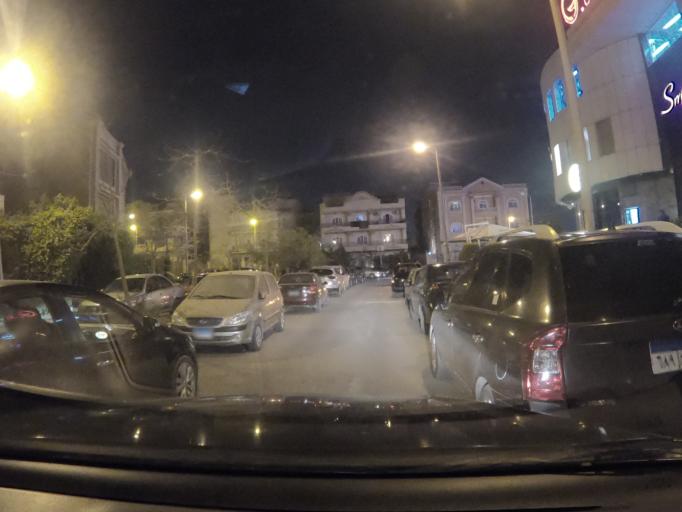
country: EG
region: Muhafazat al Qahirah
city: Cairo
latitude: 30.0138
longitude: 31.4177
